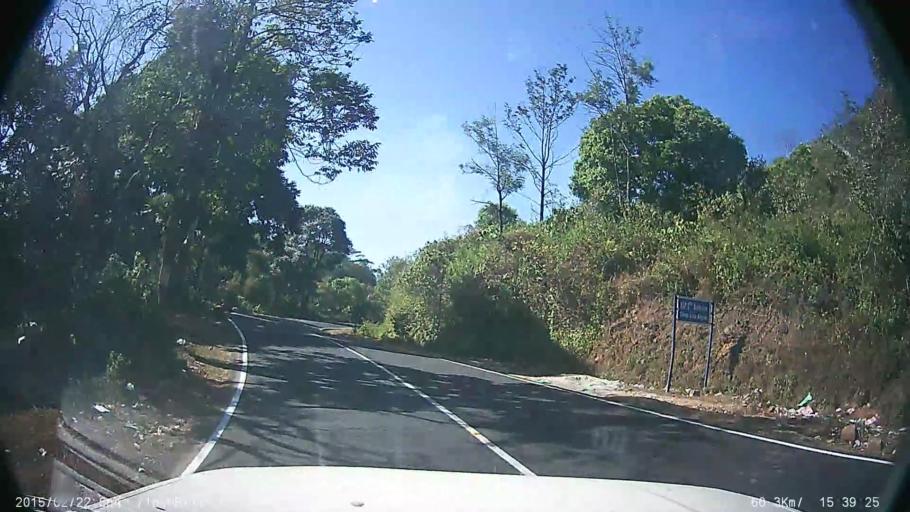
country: IN
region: Kerala
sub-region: Kottayam
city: Erattupetta
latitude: 9.5642
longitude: 76.9787
